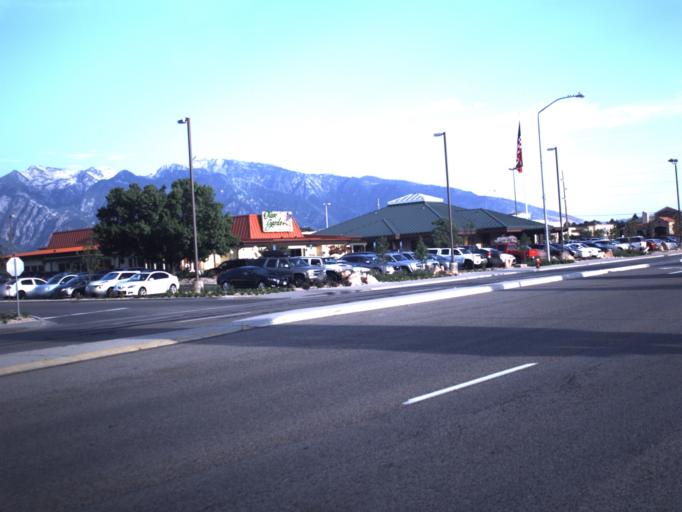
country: US
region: Utah
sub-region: Salt Lake County
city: Midvale
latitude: 40.6349
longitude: -111.8895
